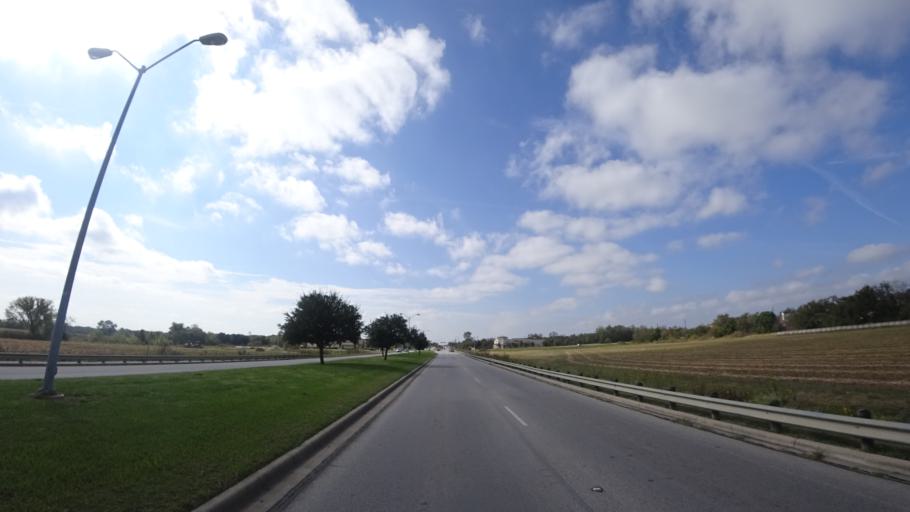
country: US
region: Texas
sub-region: Travis County
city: Pflugerville
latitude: 30.4270
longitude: -97.6252
